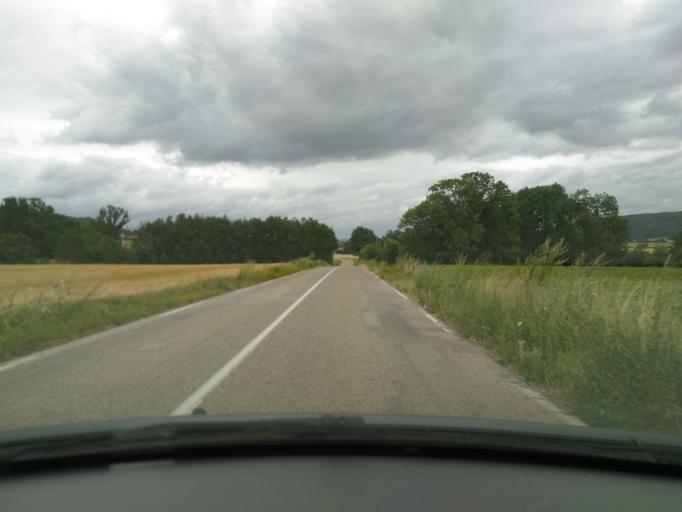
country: FR
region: Rhone-Alpes
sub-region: Departement de l'Isere
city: La Cote-Saint-Andre
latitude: 45.4301
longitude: 5.2464
